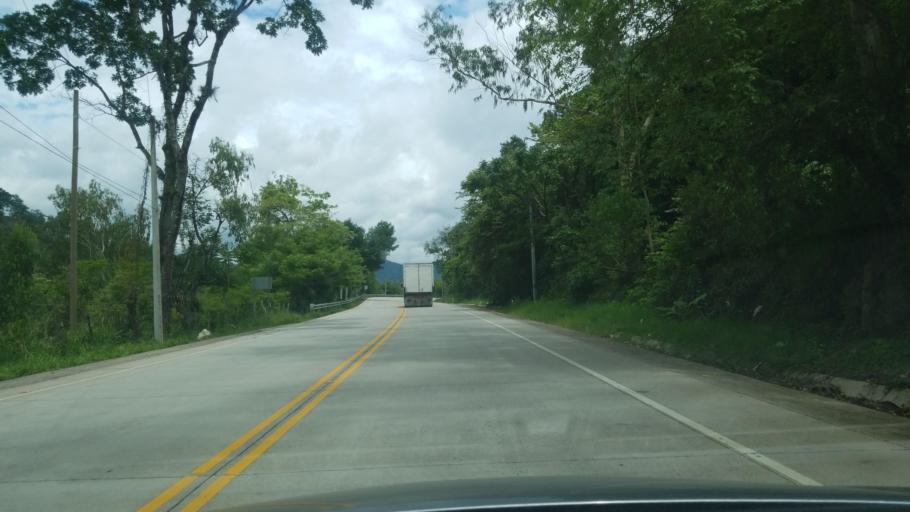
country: HN
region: Copan
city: Florida
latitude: 15.0203
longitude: -88.8328
